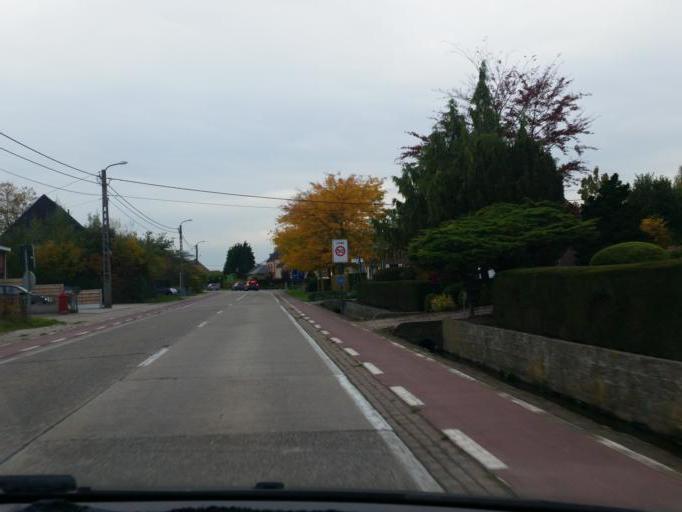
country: BE
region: Flanders
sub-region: Provincie Antwerpen
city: Putte
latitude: 51.0821
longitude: 4.5961
